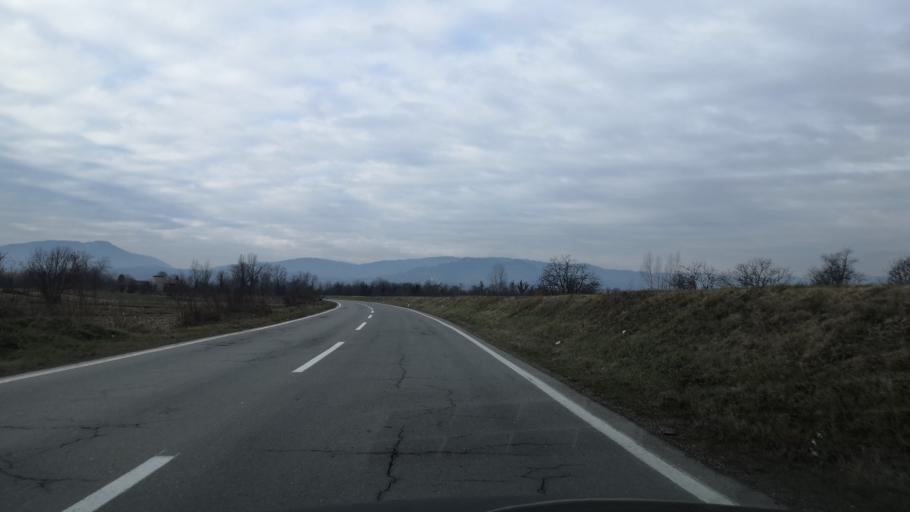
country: BA
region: Republika Srpska
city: Petkovci
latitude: 44.5222
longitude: 19.1391
